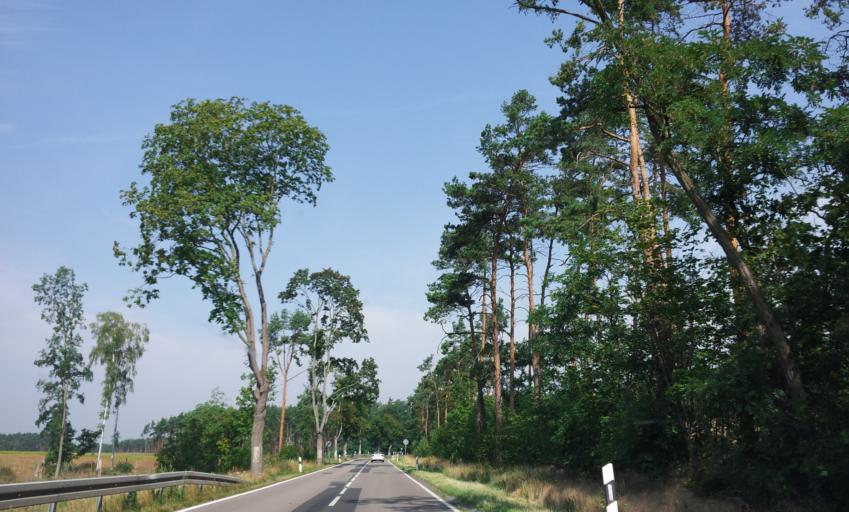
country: DE
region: Brandenburg
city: Linthe
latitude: 52.1213
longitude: 12.8104
